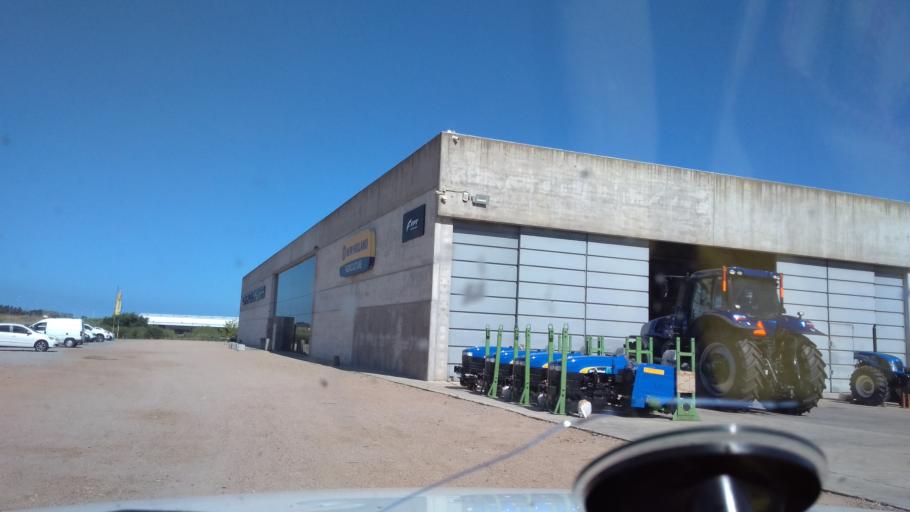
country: UY
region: Canelones
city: La Paz
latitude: -34.7936
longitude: -56.2077
